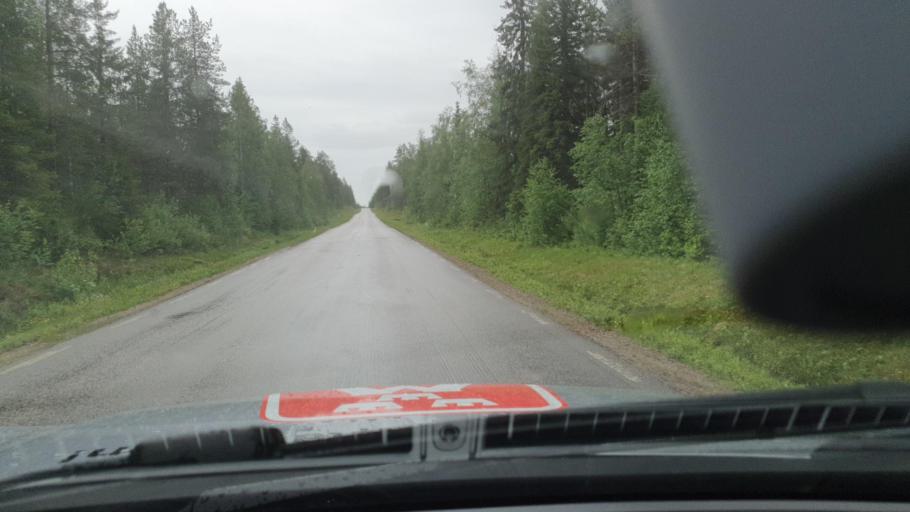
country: SE
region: Norrbotten
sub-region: Pajala Kommun
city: Pajala
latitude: 66.8338
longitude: 23.1046
